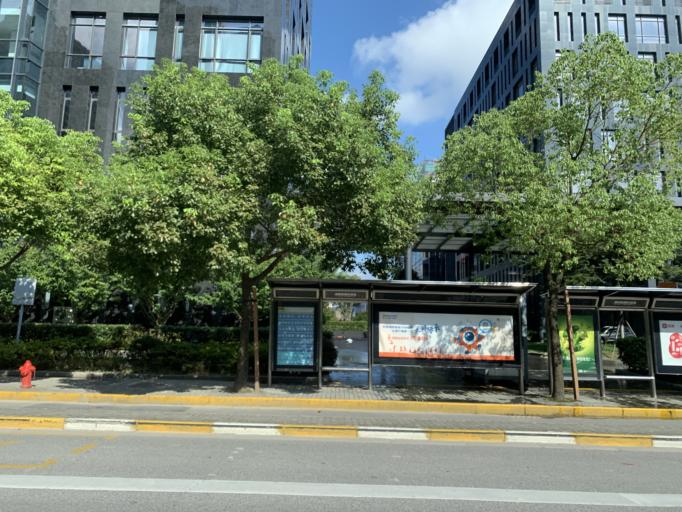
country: CN
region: Shanghai Shi
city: Pudong
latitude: 31.2129
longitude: 121.5093
